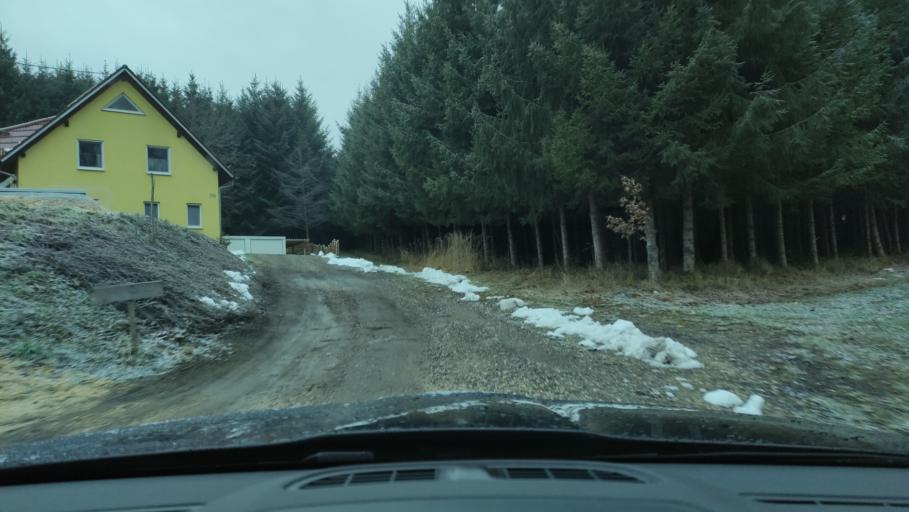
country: DE
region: Bavaria
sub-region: Swabia
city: Krumbach
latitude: 48.2538
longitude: 10.3498
